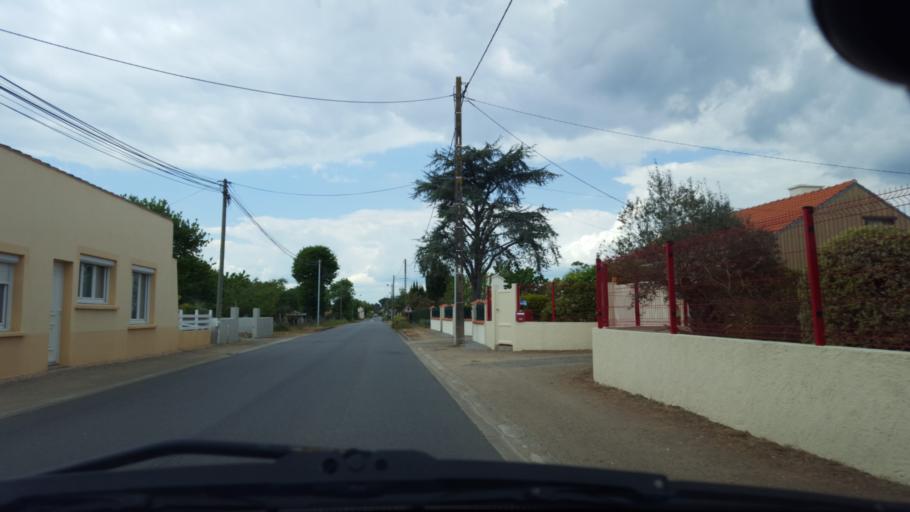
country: FR
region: Pays de la Loire
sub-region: Departement de la Loire-Atlantique
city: Saint-Philbert-de-Grand-Lieu
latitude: 47.0458
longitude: -1.6203
